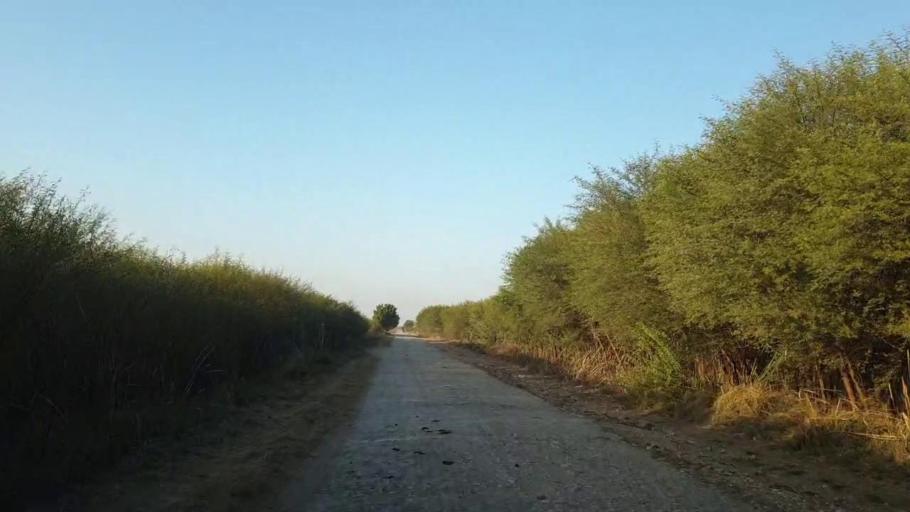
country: PK
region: Sindh
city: Mirpur Khas
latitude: 25.6672
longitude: 69.0482
